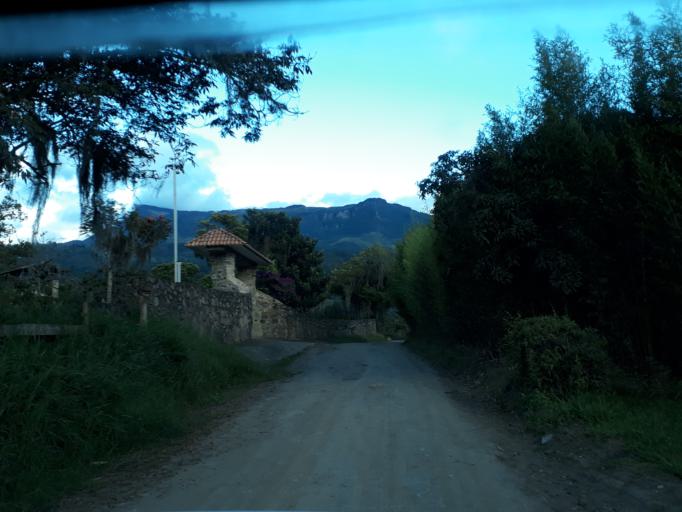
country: CO
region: Cundinamarca
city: Pacho
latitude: 5.1513
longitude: -74.1607
